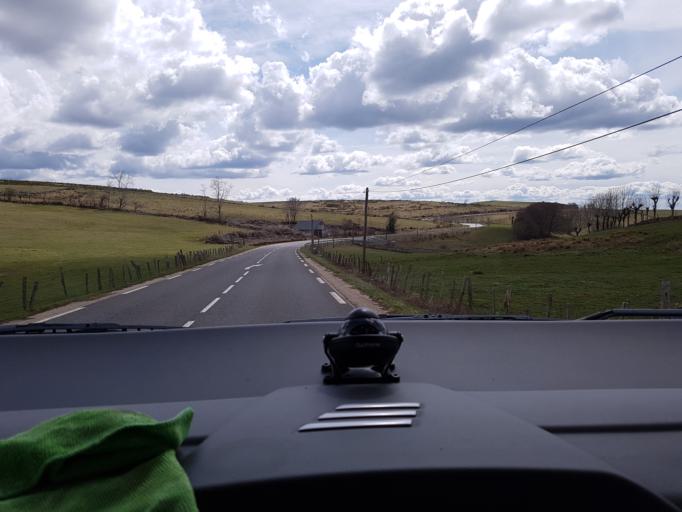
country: FR
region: Midi-Pyrenees
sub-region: Departement de l'Aveyron
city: Laguiole
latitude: 44.7221
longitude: 2.8694
